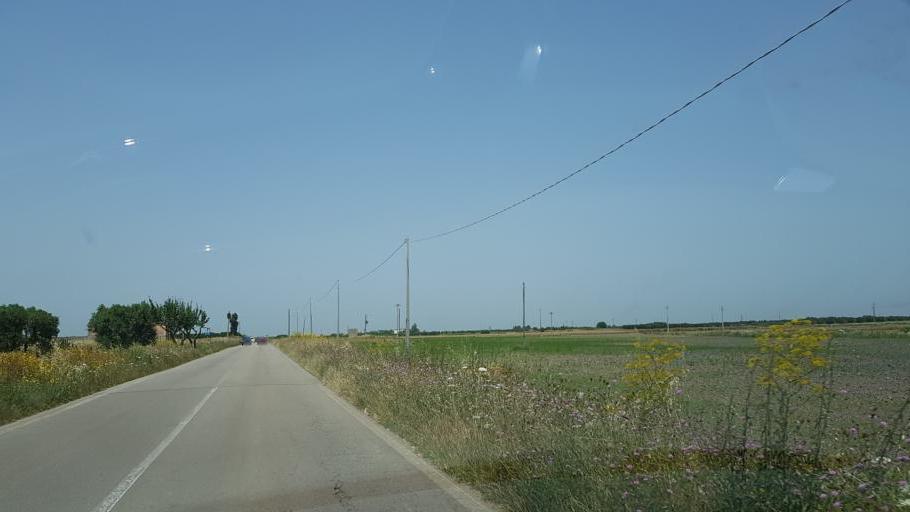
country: IT
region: Apulia
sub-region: Provincia di Brindisi
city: San Pancrazio Salentino
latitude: 40.3884
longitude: 17.8357
